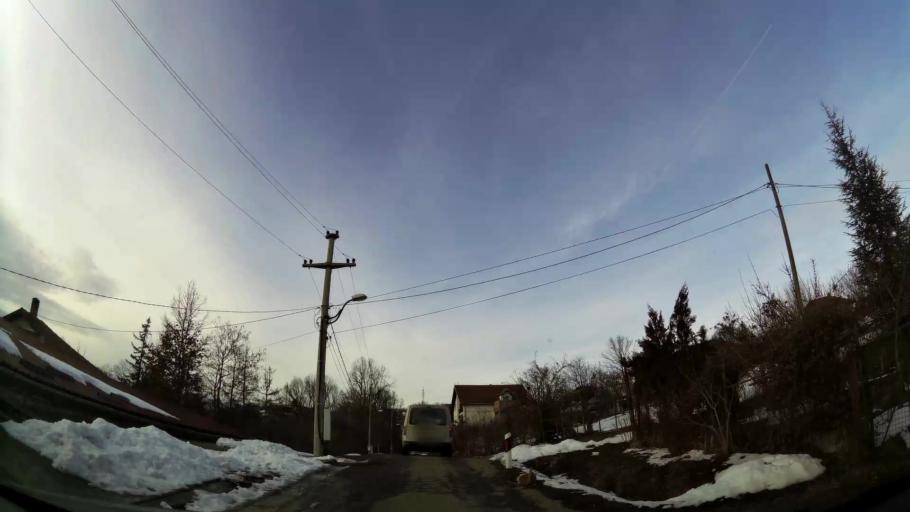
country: RS
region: Central Serbia
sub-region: Belgrade
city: Zvezdara
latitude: 44.7185
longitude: 20.5081
